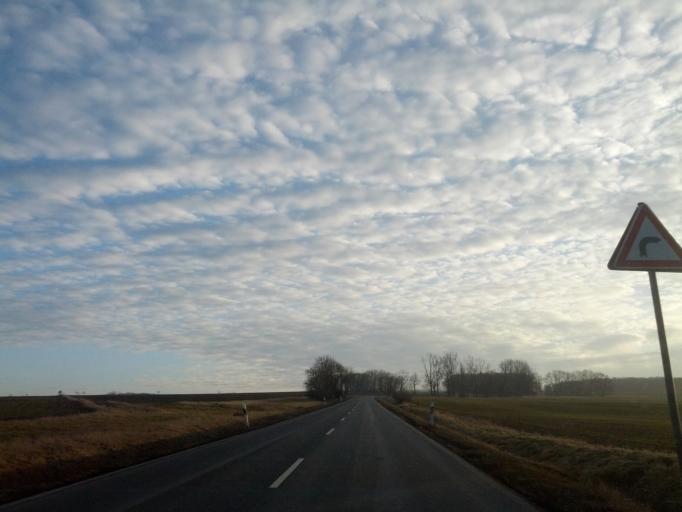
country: DE
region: Thuringia
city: Schonstedt
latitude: 51.0736
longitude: 10.5937
